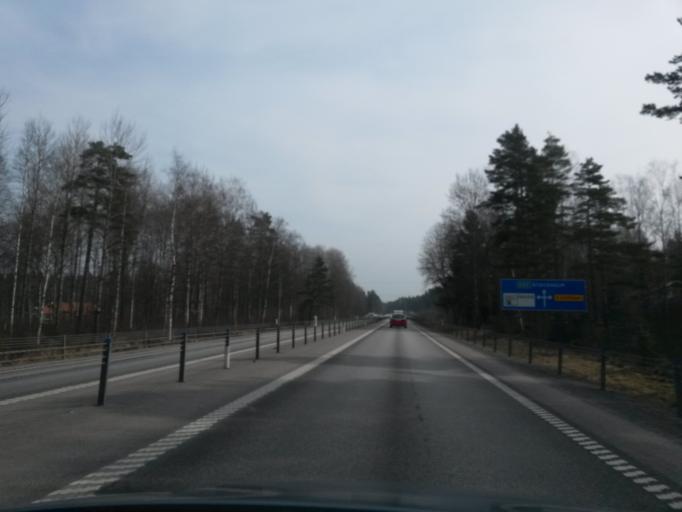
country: SE
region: OErebro
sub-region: Laxa Kommun
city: Laxa
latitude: 58.9786
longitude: 14.5998
